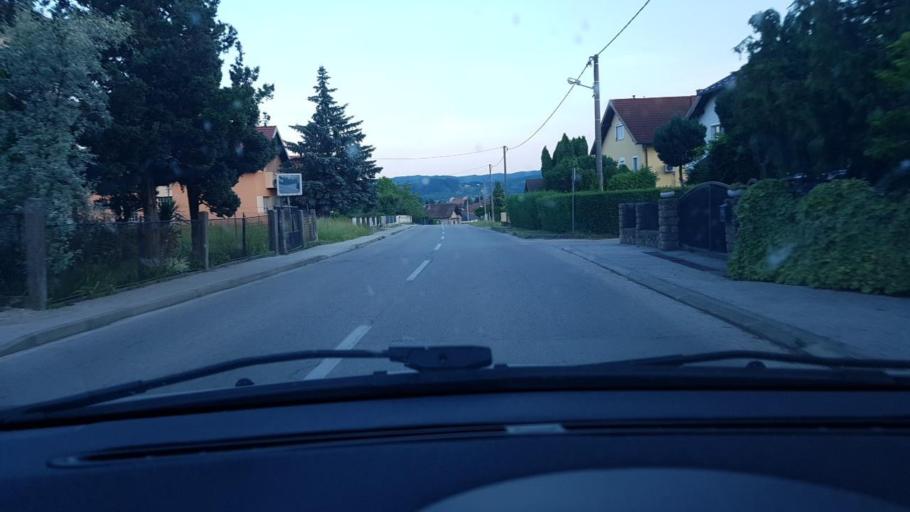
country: HR
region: Varazdinska
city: Remetinec
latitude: 46.1752
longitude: 16.3325
